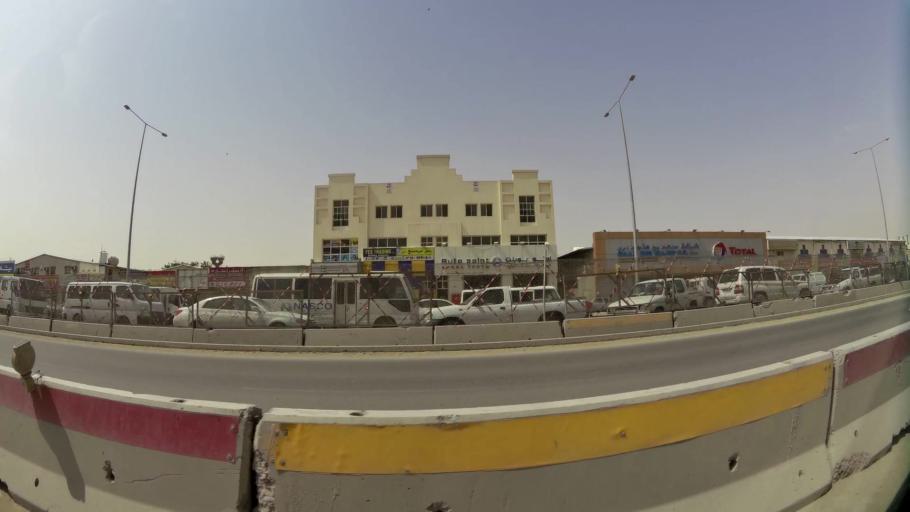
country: QA
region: Baladiyat ar Rayyan
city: Ar Rayyan
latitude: 25.2037
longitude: 51.4260
